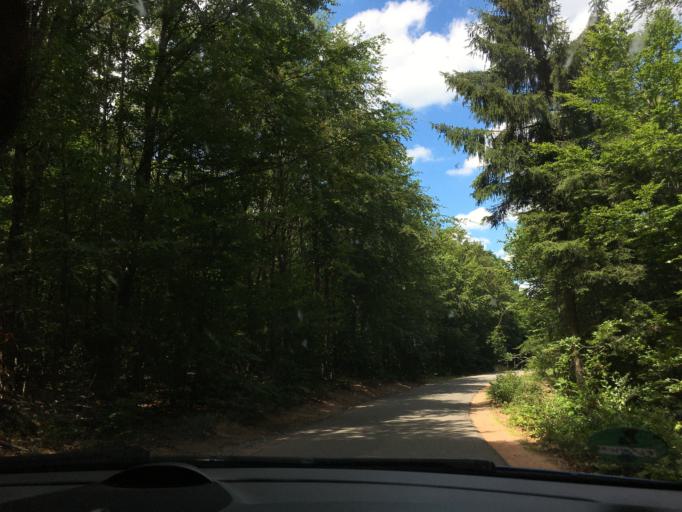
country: DE
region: Rheinland-Pfalz
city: Leimen
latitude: 49.2558
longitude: 7.8283
